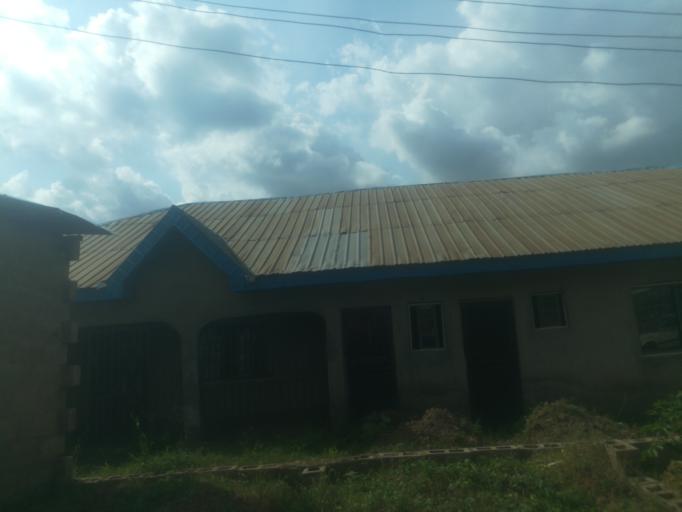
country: NG
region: Oyo
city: Ibadan
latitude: 7.3920
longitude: 3.8209
